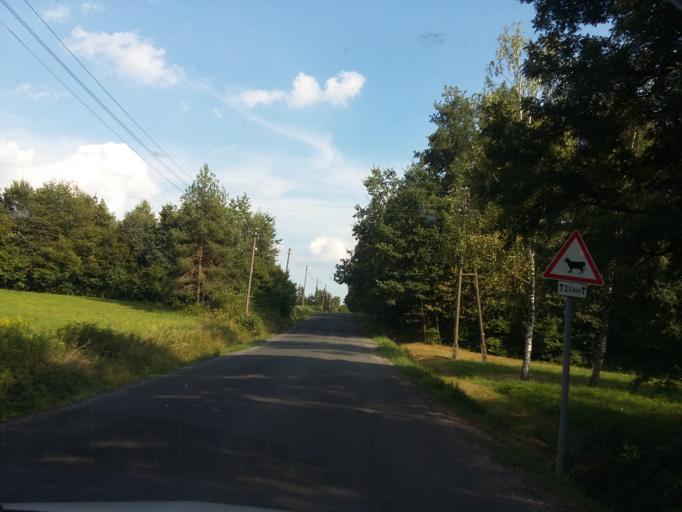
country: SI
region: Hodos-Hodos
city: Hodos
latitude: 46.8645
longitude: 16.3644
